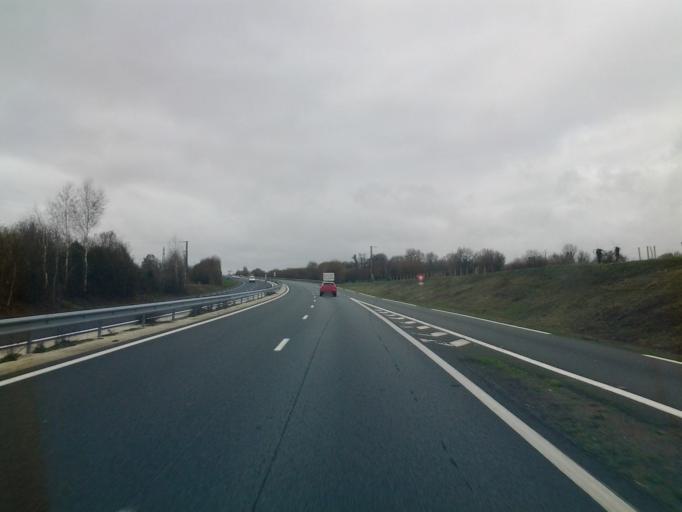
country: FR
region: Pays de la Loire
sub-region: Departement de la Vendee
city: La Chaize-le-Vicomte
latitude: 46.6614
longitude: -1.2504
